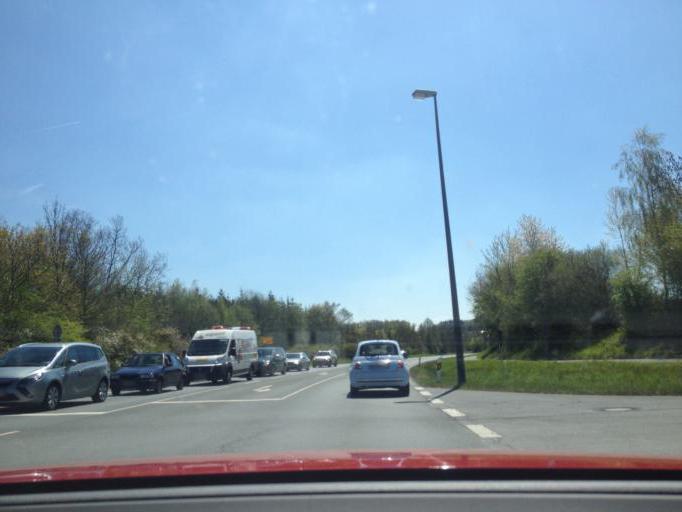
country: DE
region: Bavaria
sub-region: Upper Franconia
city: Oberkotzau
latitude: 50.2818
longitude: 11.9241
